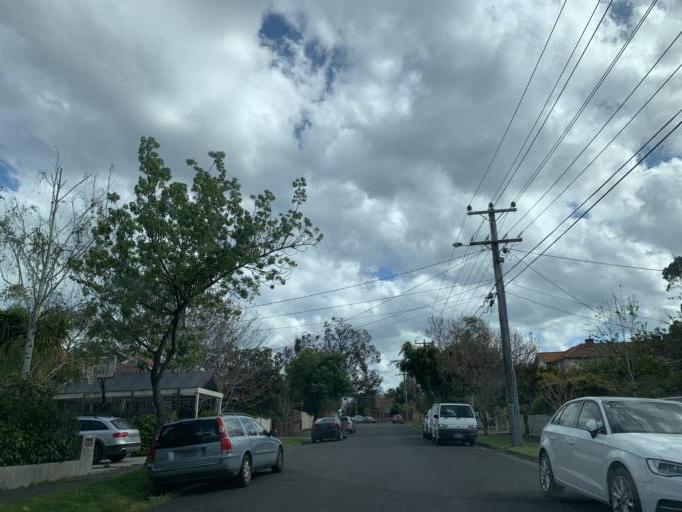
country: AU
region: Victoria
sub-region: Bayside
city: North Brighton
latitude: -37.9140
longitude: 145.0141
